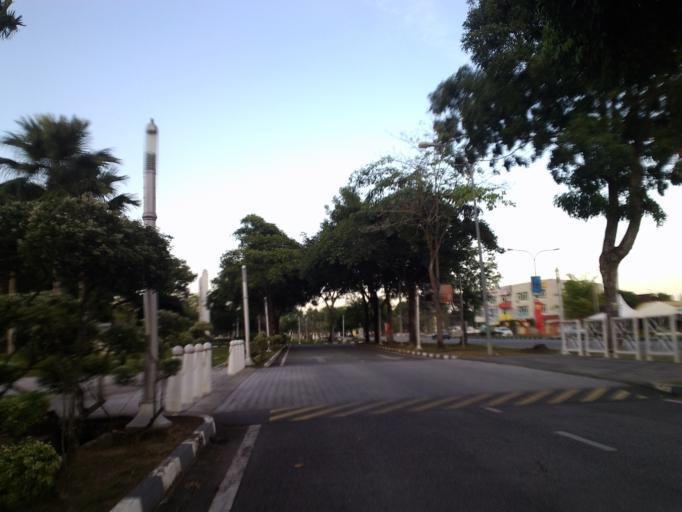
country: MY
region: Kedah
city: Alor Setar
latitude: 6.1317
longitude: 100.3885
